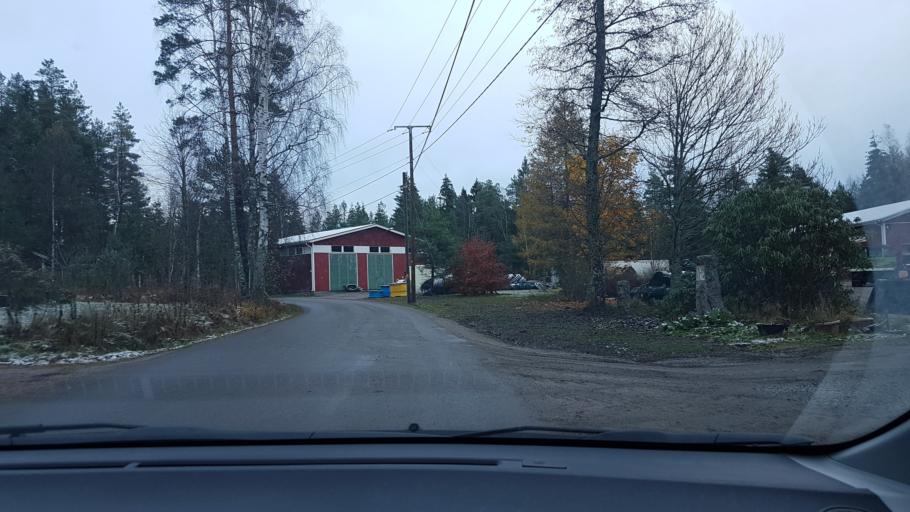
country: FI
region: Uusimaa
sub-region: Helsinki
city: Vantaa
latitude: 60.2821
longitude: 25.1568
